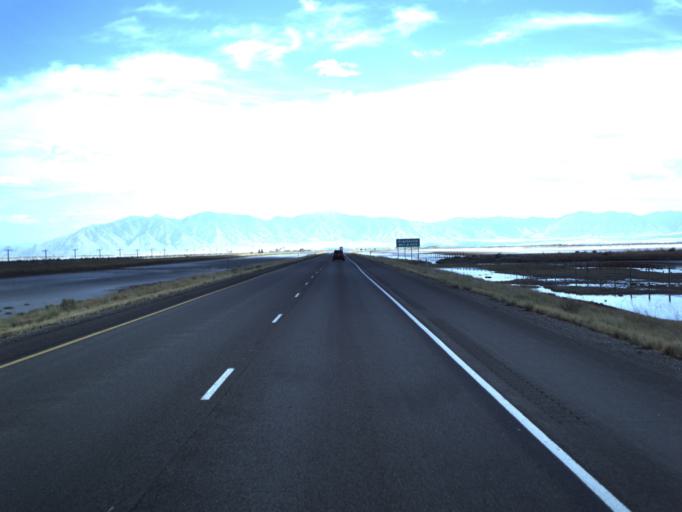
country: US
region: Utah
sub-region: Tooele County
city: Grantsville
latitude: 40.7231
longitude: -112.5657
